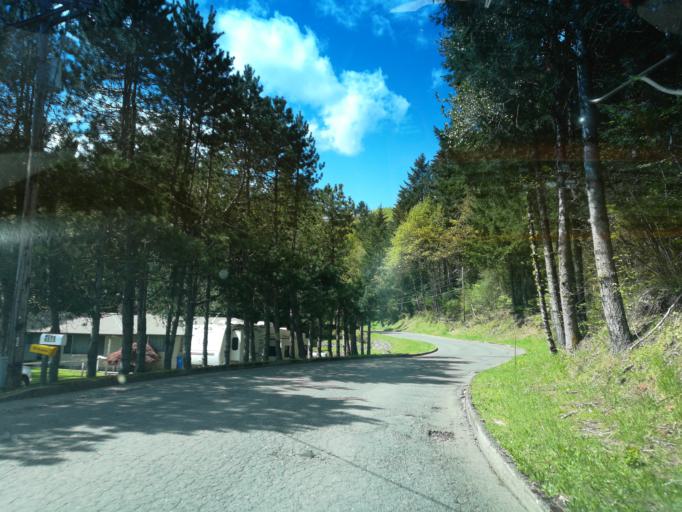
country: US
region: Oregon
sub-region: Multnomah County
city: Gresham
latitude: 45.4544
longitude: -122.4212
